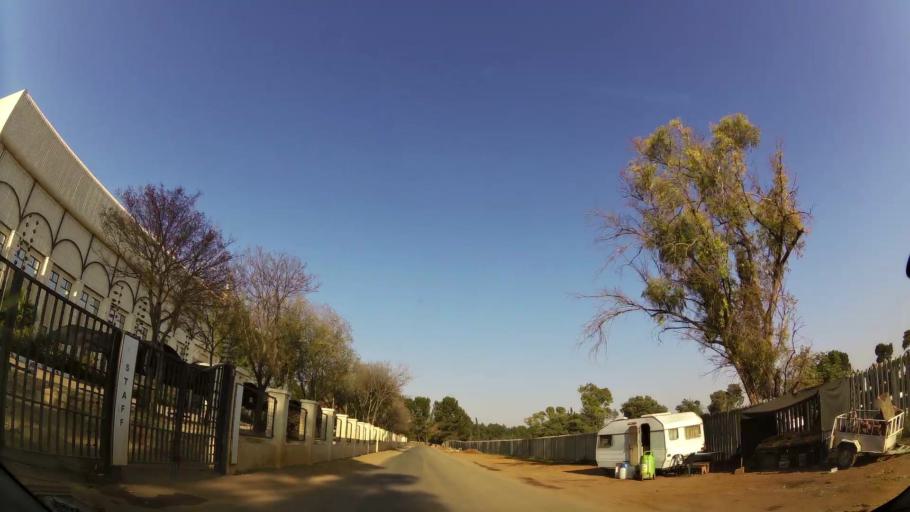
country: ZA
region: Gauteng
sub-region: City of Johannesburg Metropolitan Municipality
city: Modderfontein
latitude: -26.1524
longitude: 28.1744
